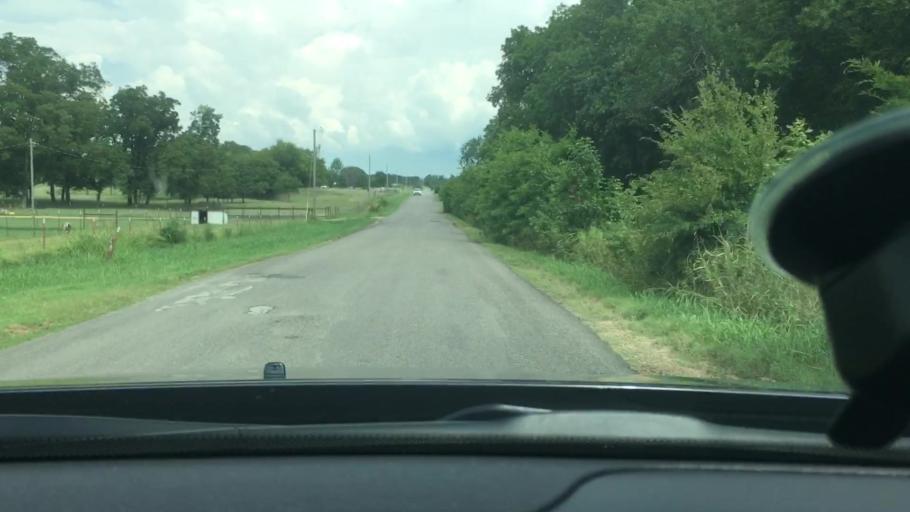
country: US
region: Oklahoma
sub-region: Carter County
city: Dickson
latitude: 34.1907
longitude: -96.8982
